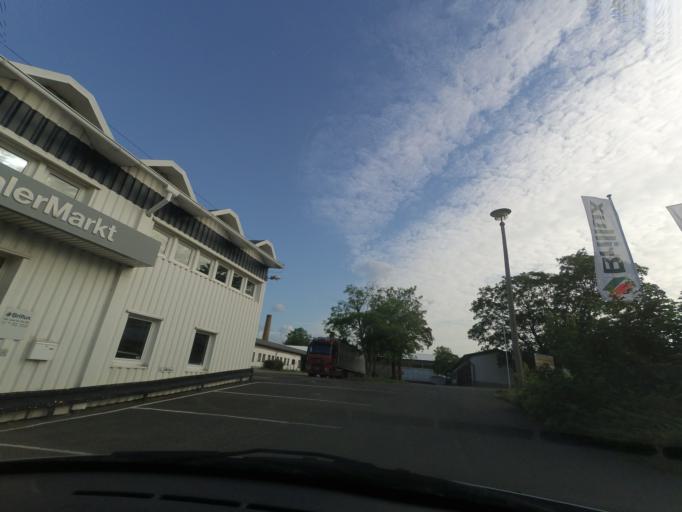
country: DE
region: Saxony
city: Kreischa
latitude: 50.9928
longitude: 13.7987
